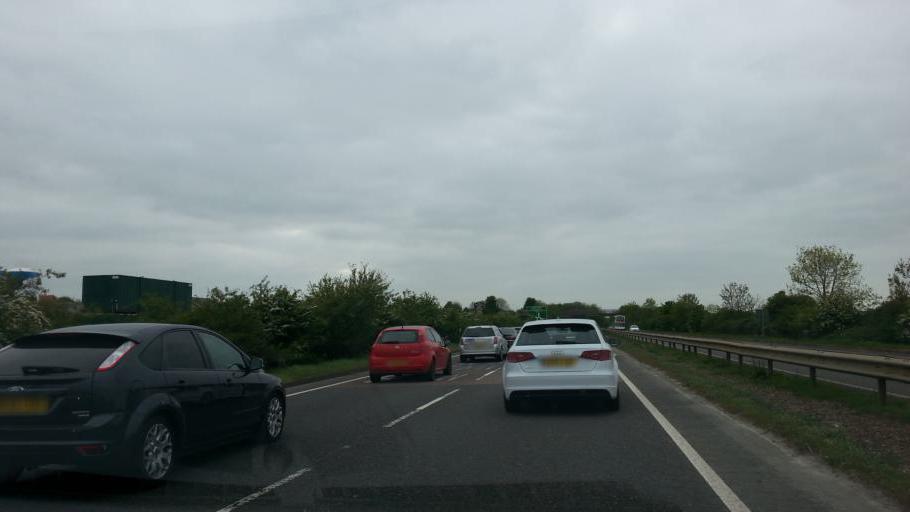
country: GB
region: England
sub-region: Lincolnshire
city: Leasingham
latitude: 53.0131
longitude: -0.4164
